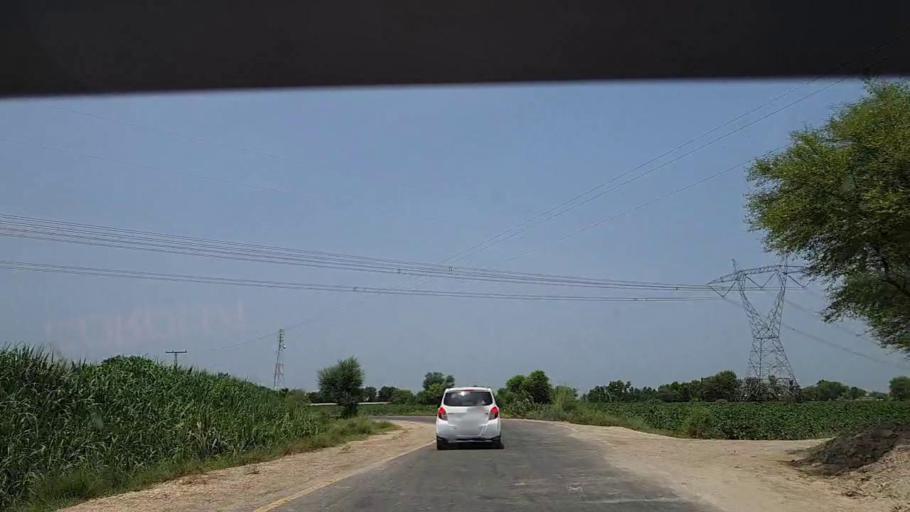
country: PK
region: Sindh
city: Adilpur
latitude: 27.8731
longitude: 69.2802
